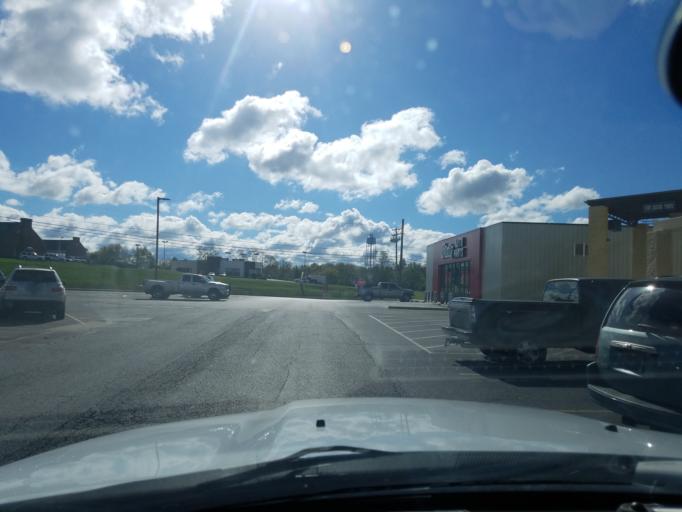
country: US
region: Kentucky
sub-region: Lincoln County
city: Stanford
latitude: 37.5403
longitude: -84.6535
